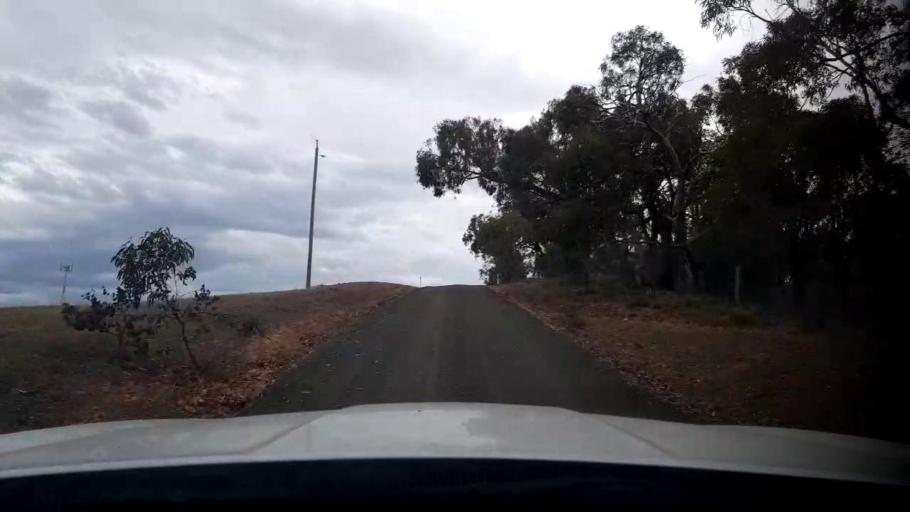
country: AU
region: Victoria
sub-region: Whittlesea
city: Whittlesea
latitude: -37.4868
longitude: 145.0485
